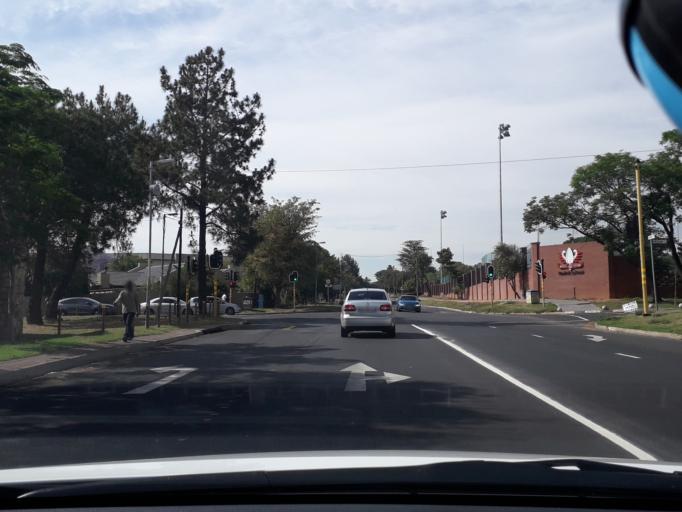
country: ZA
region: Gauteng
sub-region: City of Johannesburg Metropolitan Municipality
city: Modderfontein
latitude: -26.0733
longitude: 28.0596
